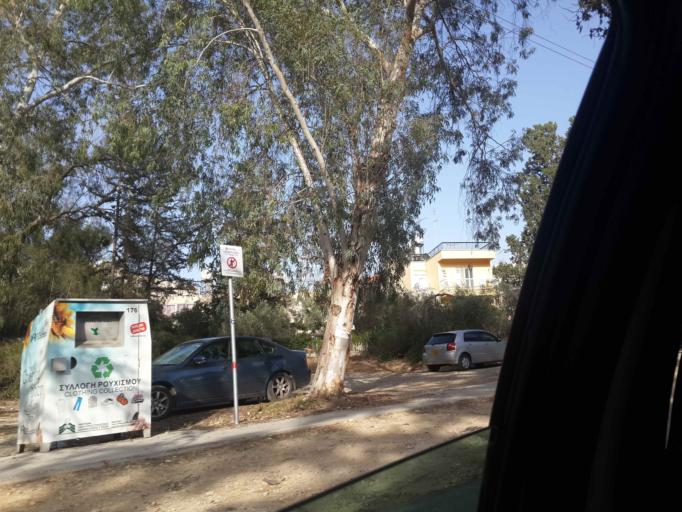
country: CY
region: Lefkosia
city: Nicosia
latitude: 35.1598
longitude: 33.3492
